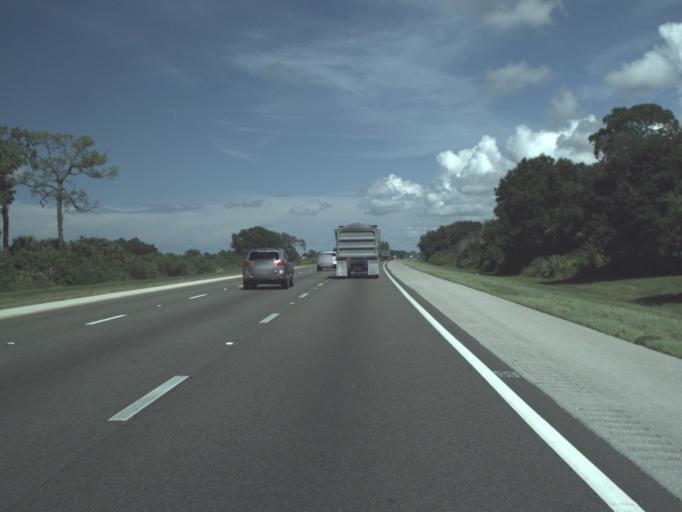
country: US
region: Florida
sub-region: Sarasota County
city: Laurel
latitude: 27.1713
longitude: -82.4331
